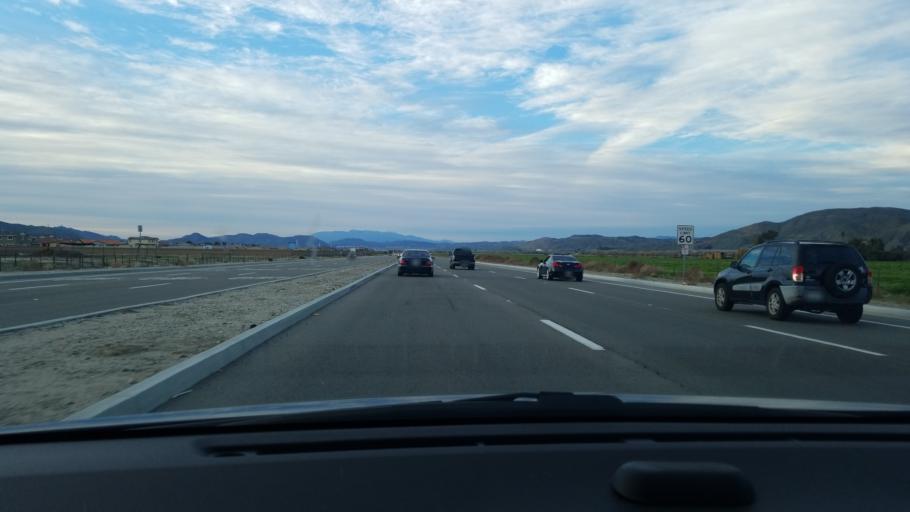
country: US
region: California
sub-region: Riverside County
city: San Jacinto
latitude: 33.8117
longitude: -116.9863
